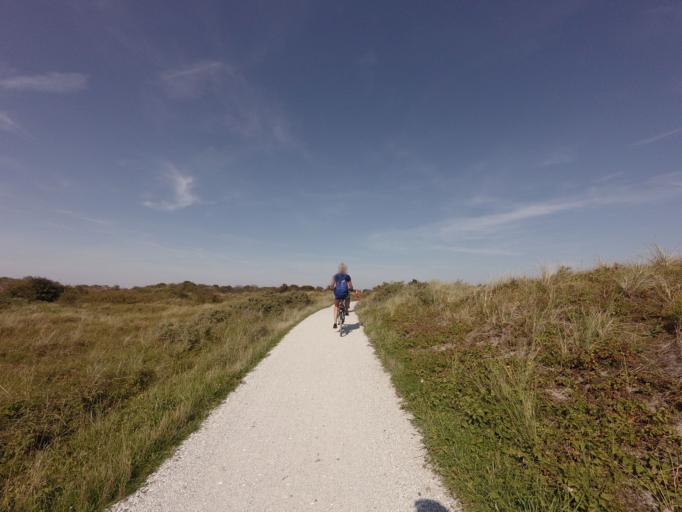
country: NL
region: Friesland
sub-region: Gemeente Schiermonnikoog
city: Schiermonnikoog
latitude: 53.4760
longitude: 6.1392
